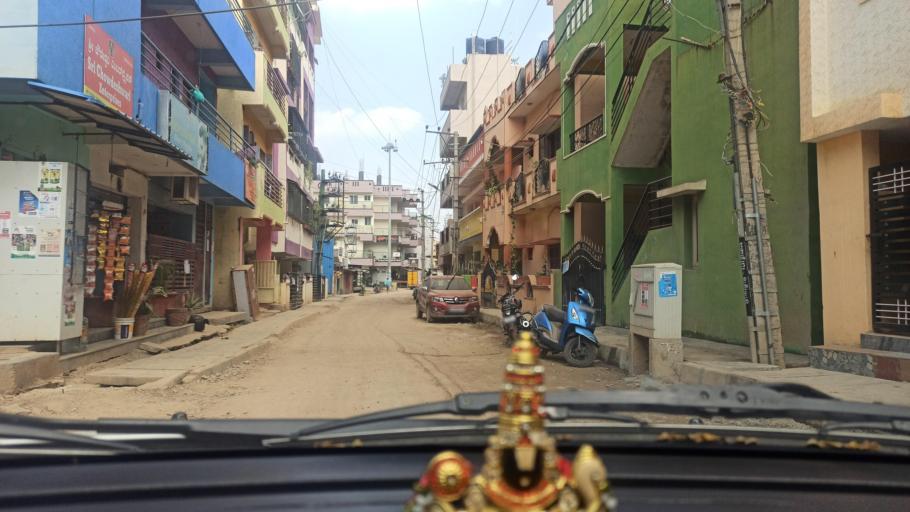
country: IN
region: Karnataka
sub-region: Bangalore Urban
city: Bangalore
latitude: 13.0188
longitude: 77.6656
